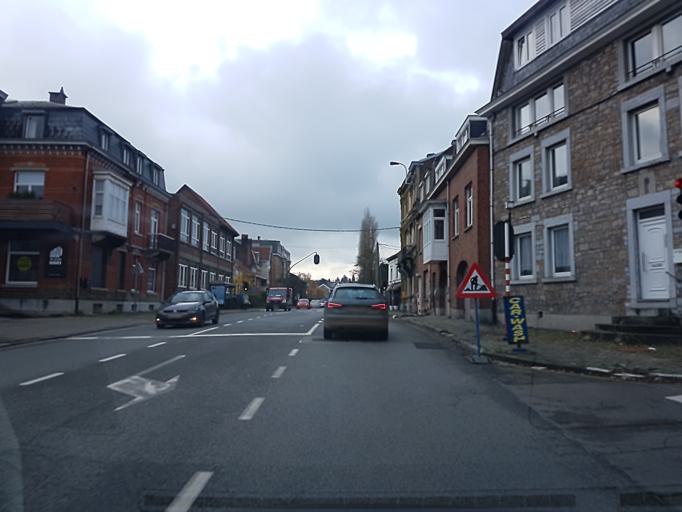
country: BE
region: Wallonia
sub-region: Province de Liege
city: Verviers
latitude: 50.5767
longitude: 5.8658
